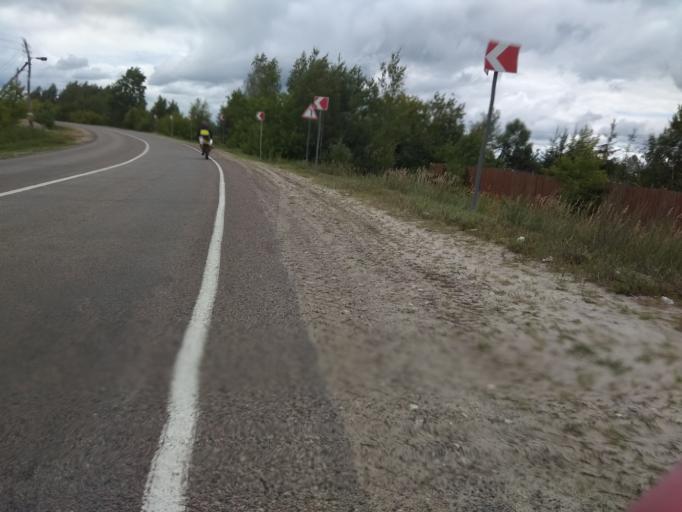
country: RU
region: Moskovskaya
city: Kerva
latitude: 55.5868
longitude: 39.7005
